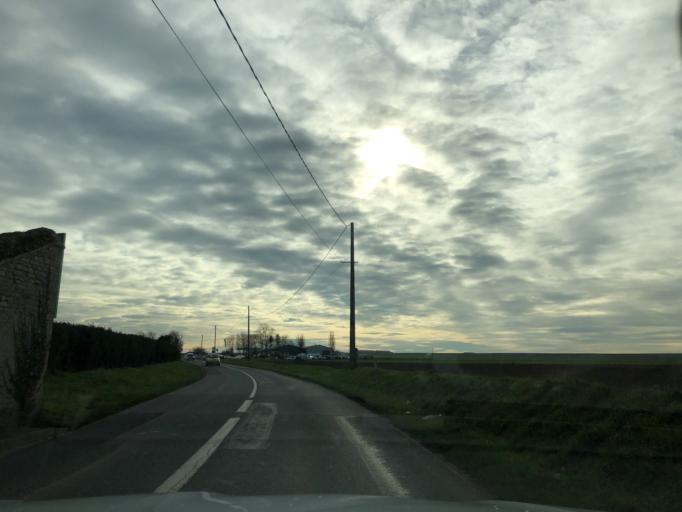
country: FR
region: Lower Normandy
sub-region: Departement du Calvados
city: Hermanville-sur-Mer
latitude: 49.2804
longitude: -0.3178
